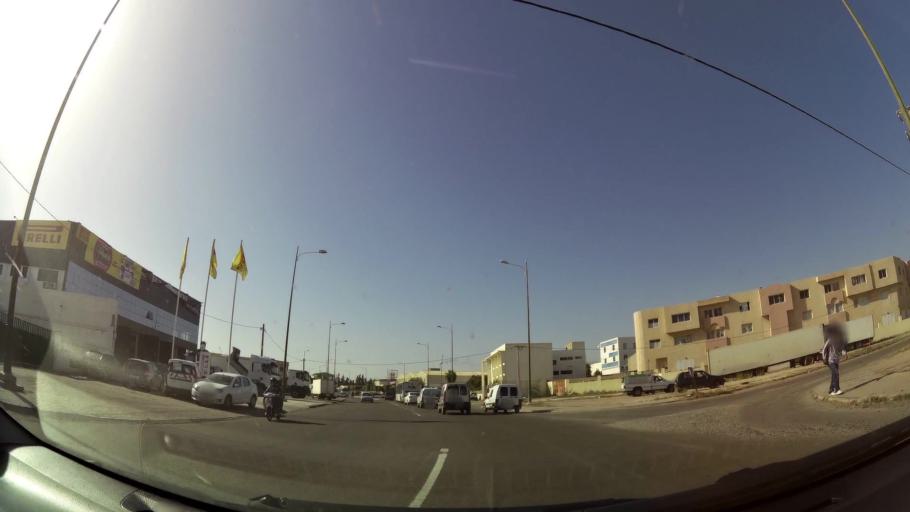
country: MA
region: Souss-Massa-Draa
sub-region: Inezgane-Ait Mellou
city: Inezgane
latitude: 30.3822
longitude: -9.5187
